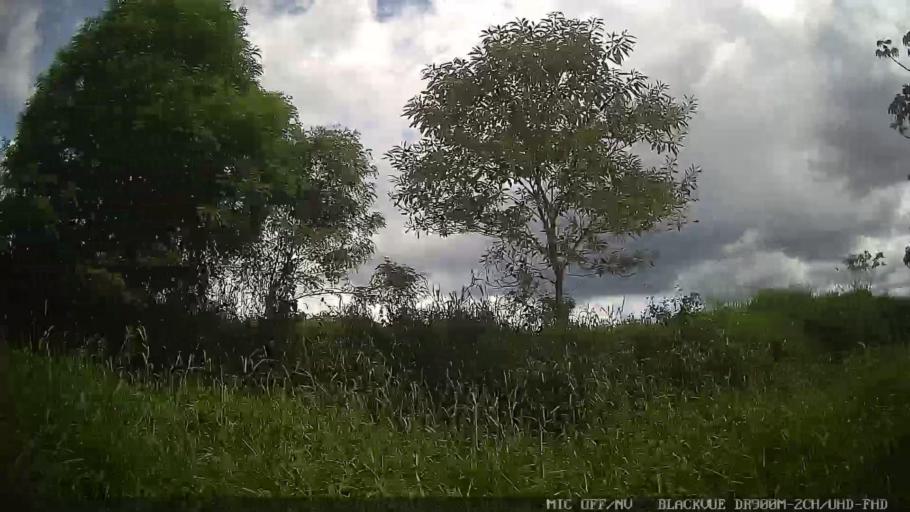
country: BR
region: Sao Paulo
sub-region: Rio Grande Da Serra
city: Rio Grande da Serra
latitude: -23.6970
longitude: -46.2746
